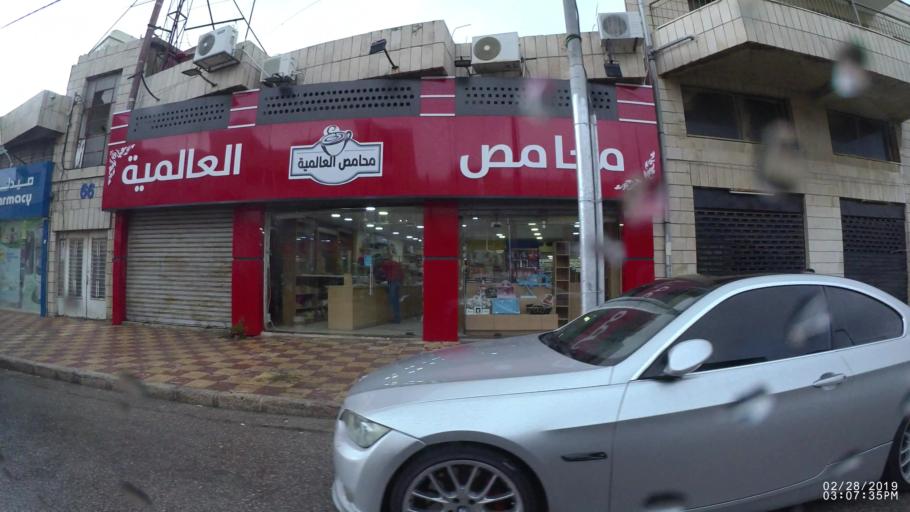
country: JO
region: Amman
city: Al Jubayhah
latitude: 32.0262
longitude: 35.8641
